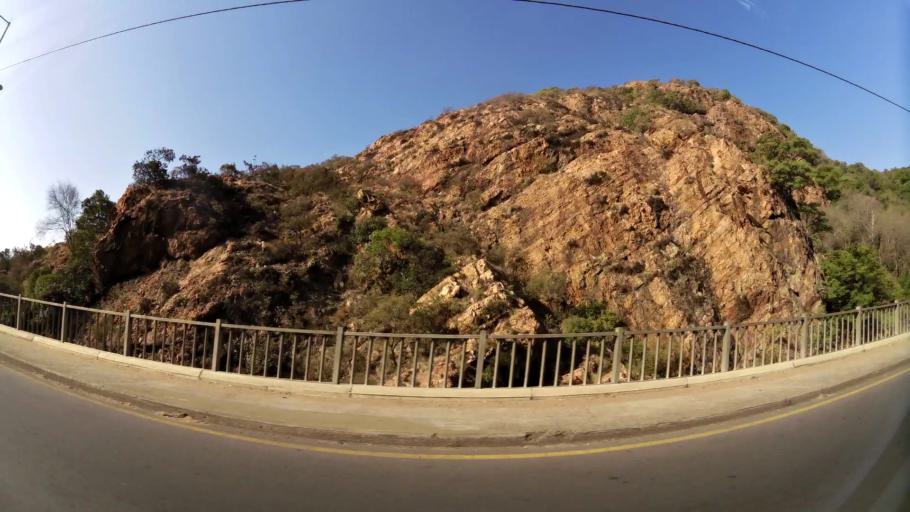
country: ZA
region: Gauteng
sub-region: City of Tshwane Metropolitan Municipality
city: Pretoria
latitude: -25.6897
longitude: 28.1875
